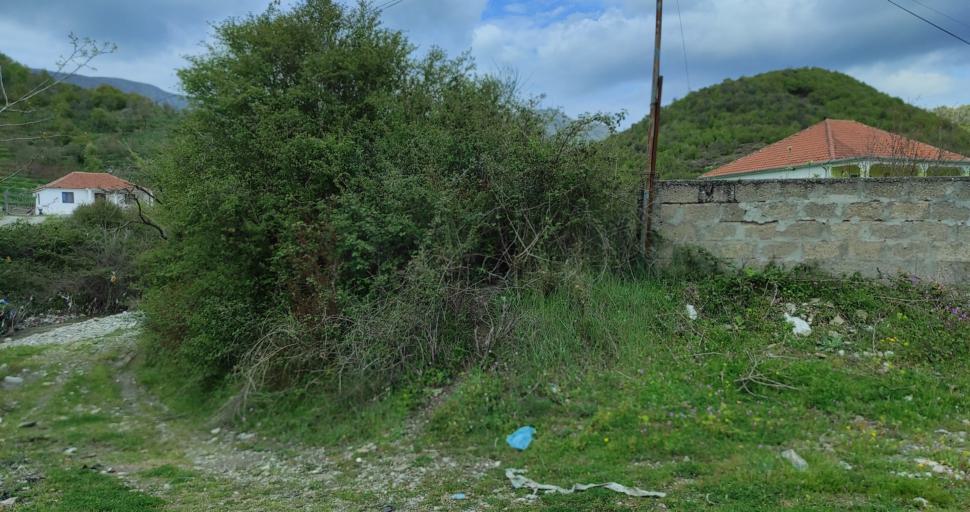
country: AL
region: Shkoder
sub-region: Rrethi i Shkodres
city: Dajc
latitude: 42.0283
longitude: 19.4181
